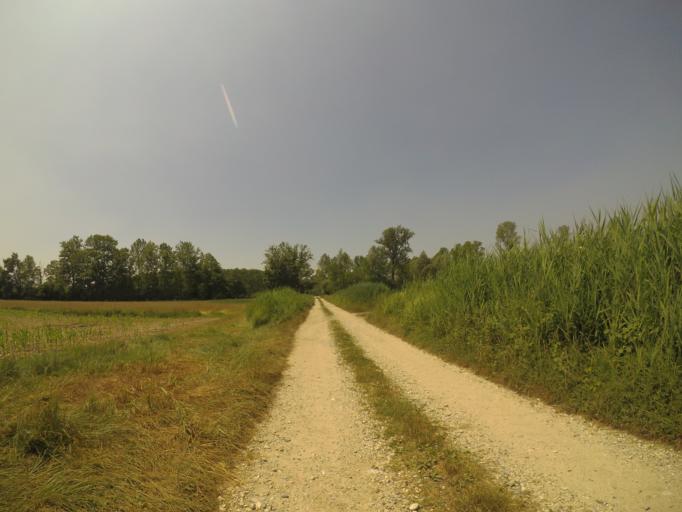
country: IT
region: Friuli Venezia Giulia
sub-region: Provincia di Udine
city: Bertiolo
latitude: 45.9177
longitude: 13.0433
